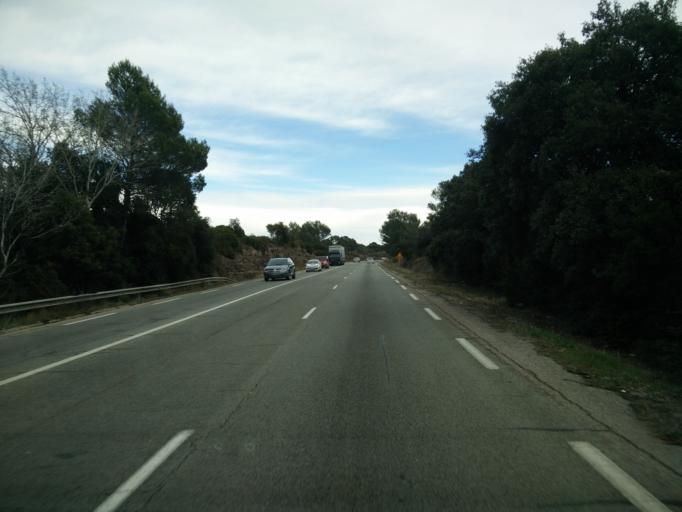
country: FR
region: Provence-Alpes-Cote d'Azur
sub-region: Departement du Var
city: Roquebrune-sur-Argens
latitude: 43.4661
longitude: 6.6163
